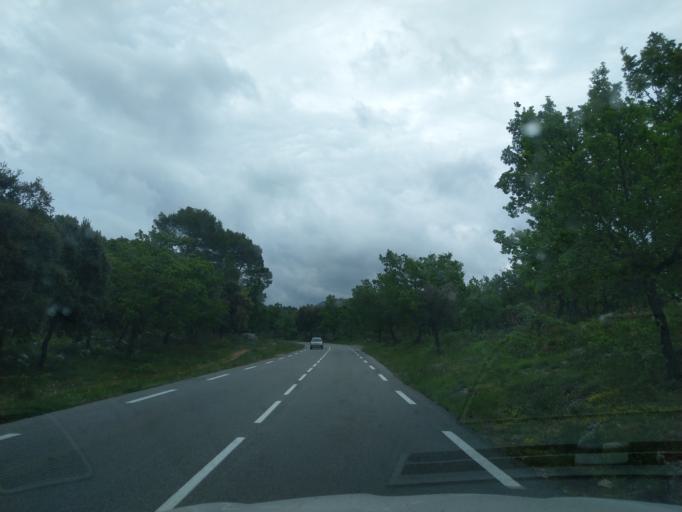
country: FR
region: Provence-Alpes-Cote d'Azur
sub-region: Departement du Var
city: Signes
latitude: 43.2750
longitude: 5.7963
